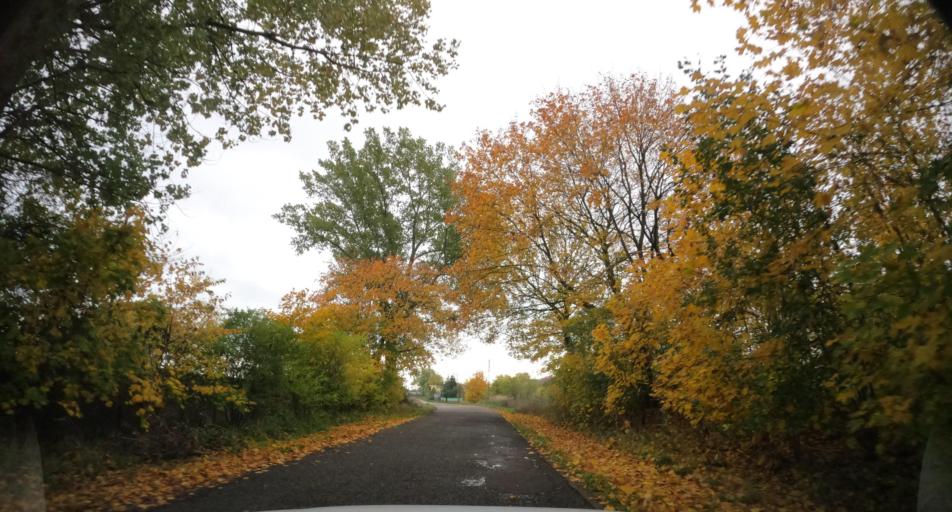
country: PL
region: West Pomeranian Voivodeship
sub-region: Powiat kamienski
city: Wolin
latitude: 53.8676
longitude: 14.5875
